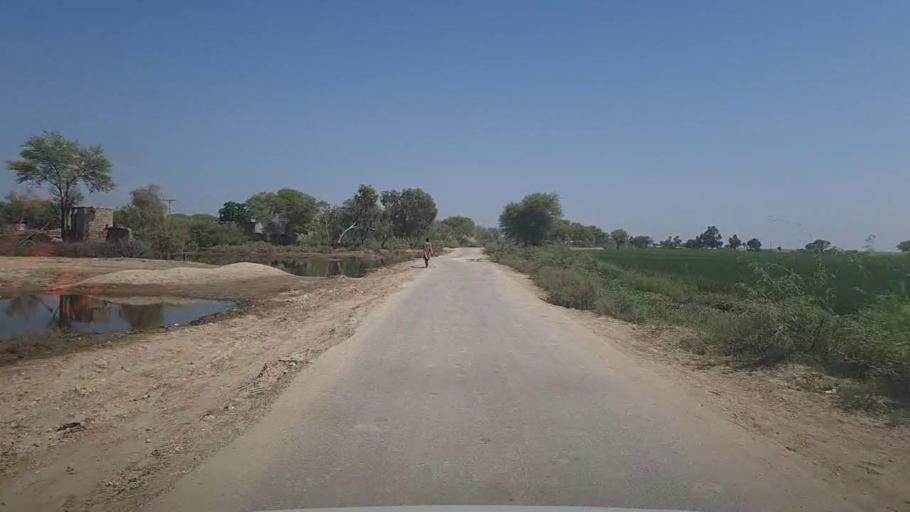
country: PK
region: Sindh
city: Kashmor
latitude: 28.2846
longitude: 69.4366
